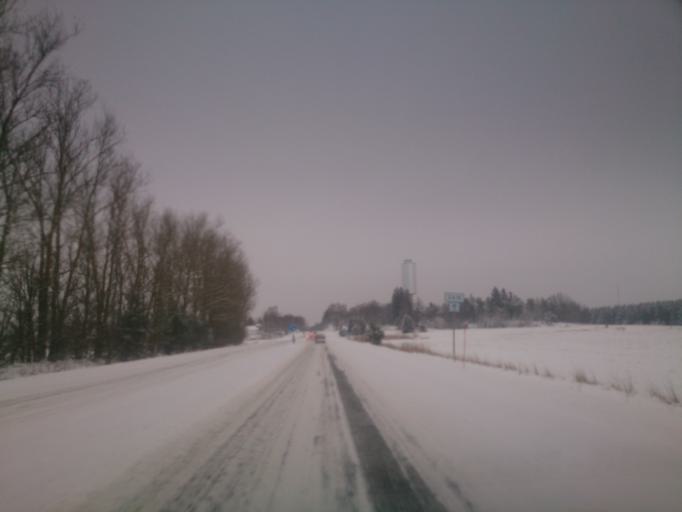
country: SE
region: OEstergoetland
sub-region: Norrkopings Kommun
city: Kimstad
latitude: 58.4993
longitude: 15.9685
